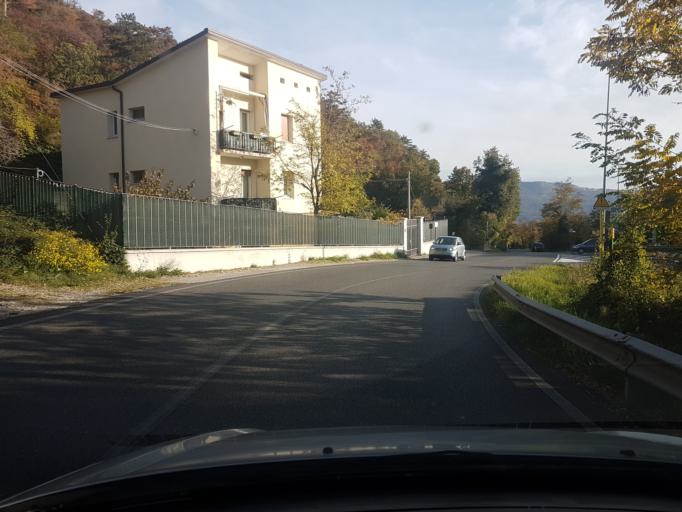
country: IT
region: Friuli Venezia Giulia
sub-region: Provincia di Trieste
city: Domio
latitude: 45.6336
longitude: 13.8403
